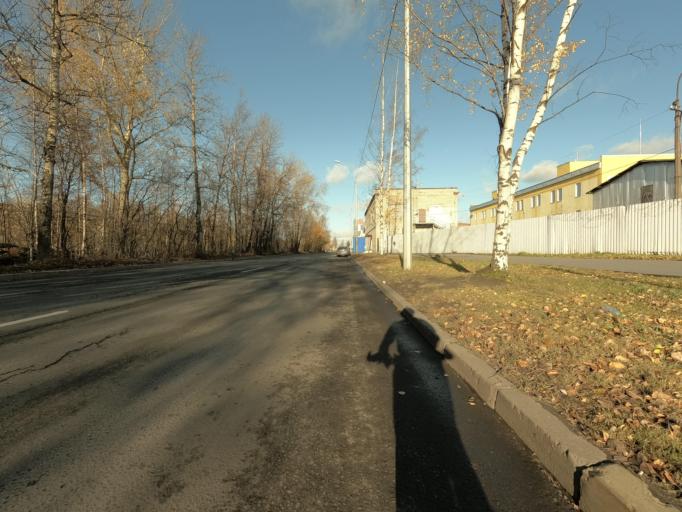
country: RU
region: St.-Petersburg
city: Krasnogvargeisky
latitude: 59.9495
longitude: 30.4479
